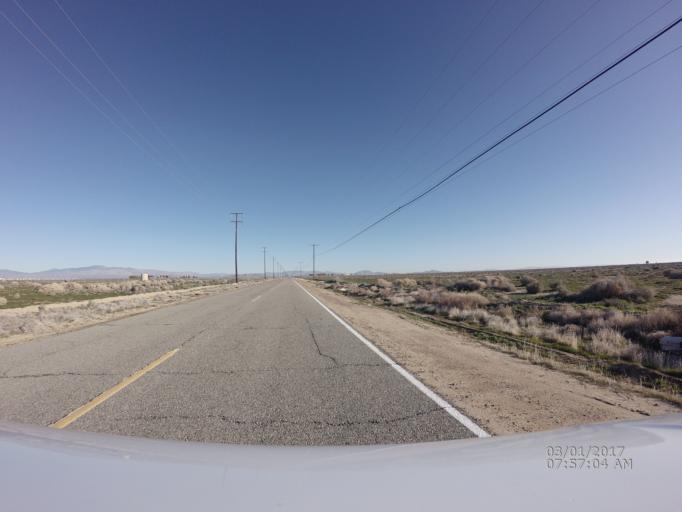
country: US
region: California
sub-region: Los Angeles County
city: Quartz Hill
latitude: 34.7634
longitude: -118.2547
